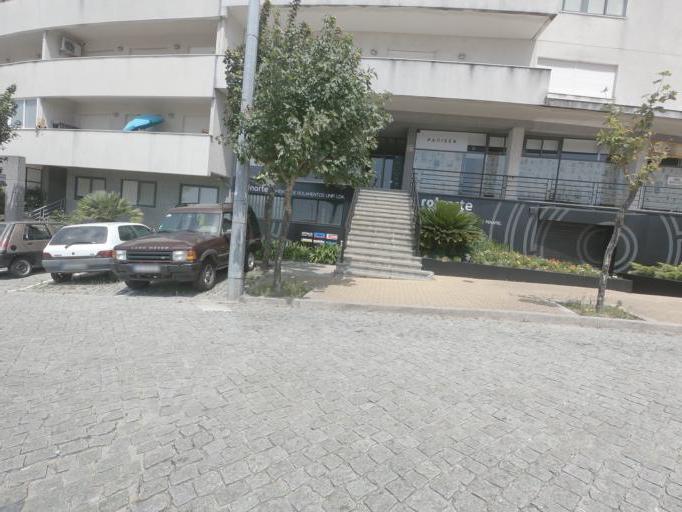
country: PT
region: Porto
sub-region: Penafiel
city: Penafiel
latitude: 41.1957
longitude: -8.2960
